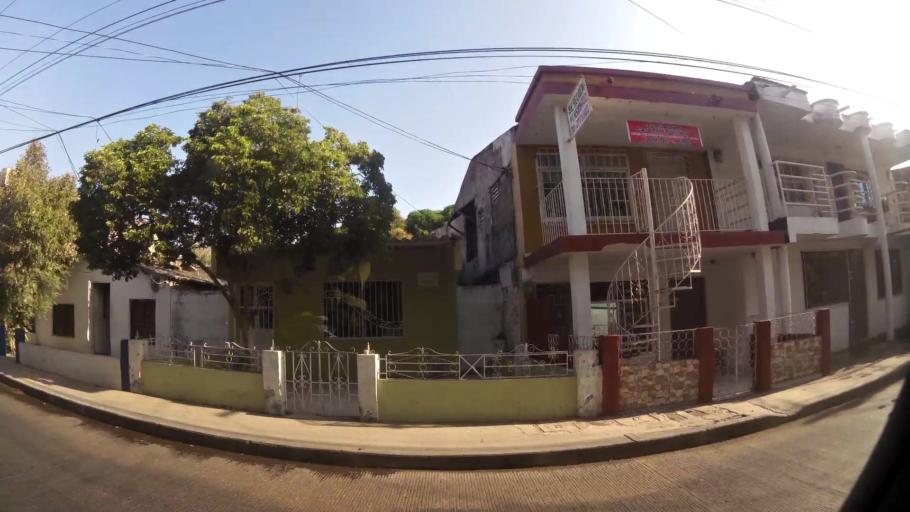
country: CO
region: Bolivar
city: Cartagena
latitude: 10.4018
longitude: -75.5037
